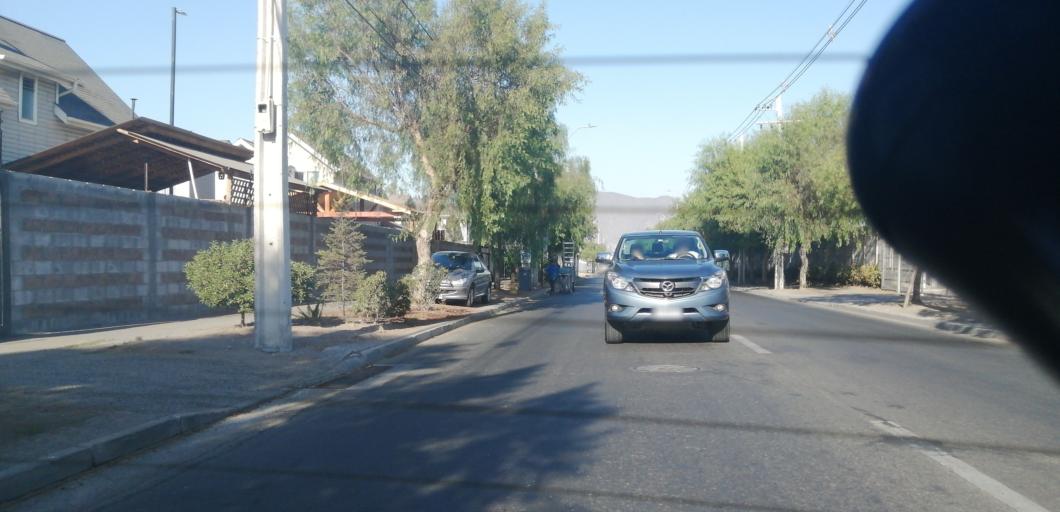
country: CL
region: Santiago Metropolitan
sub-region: Provincia de Santiago
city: Lo Prado
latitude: -33.4340
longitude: -70.7808
